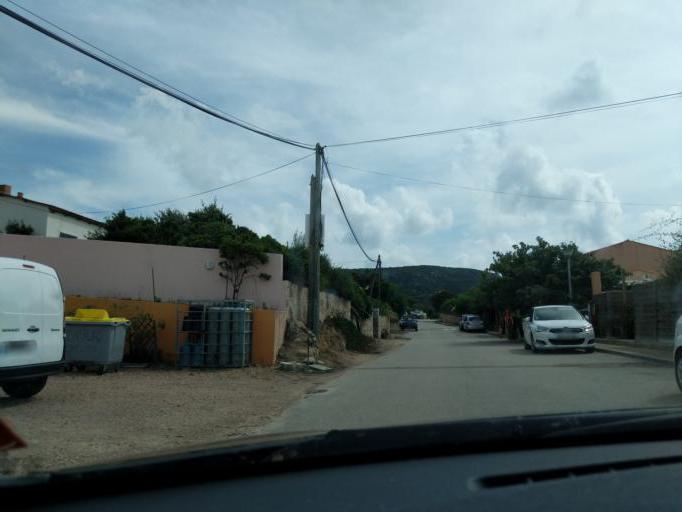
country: FR
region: Corsica
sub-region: Departement de la Corse-du-Sud
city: Propriano
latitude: 41.5408
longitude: 8.8518
